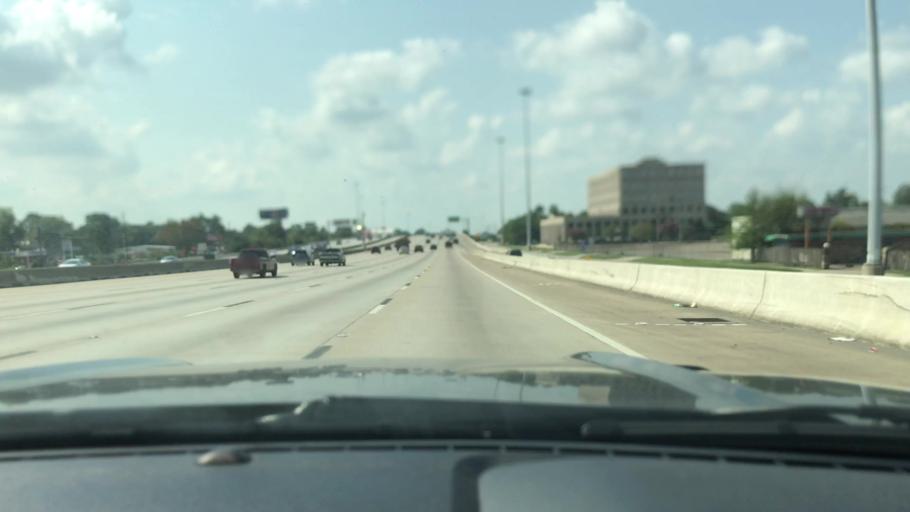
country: US
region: Texas
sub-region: Harris County
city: Houston
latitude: 29.8464
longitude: -95.3340
